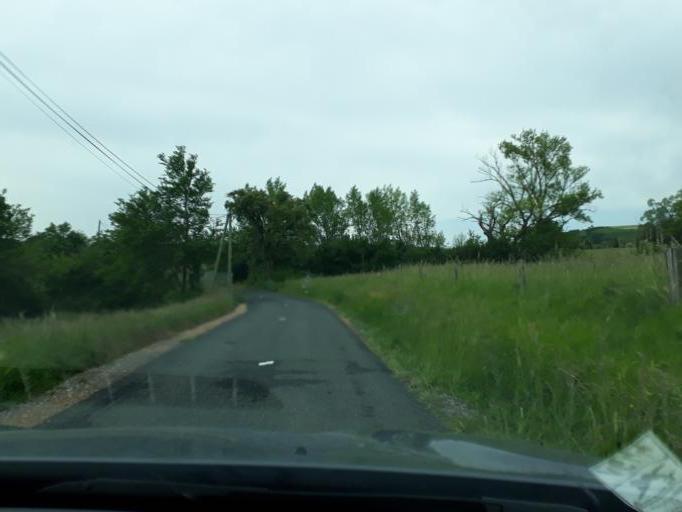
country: FR
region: Languedoc-Roussillon
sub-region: Departement de l'Herault
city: Lodeve
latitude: 43.8337
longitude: 3.2761
